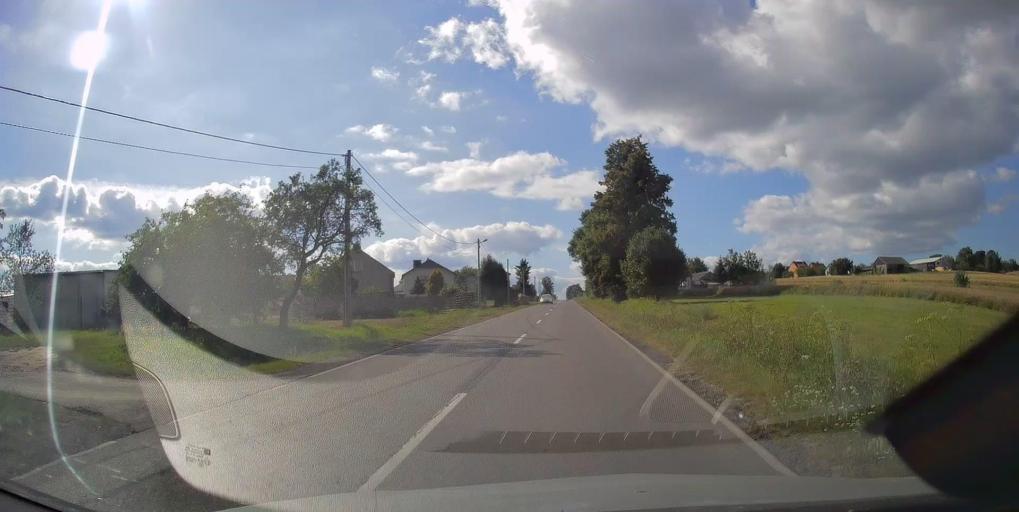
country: PL
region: Swietokrzyskie
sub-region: Powiat kielecki
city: Bodzentyn
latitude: 50.9690
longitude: 20.8854
